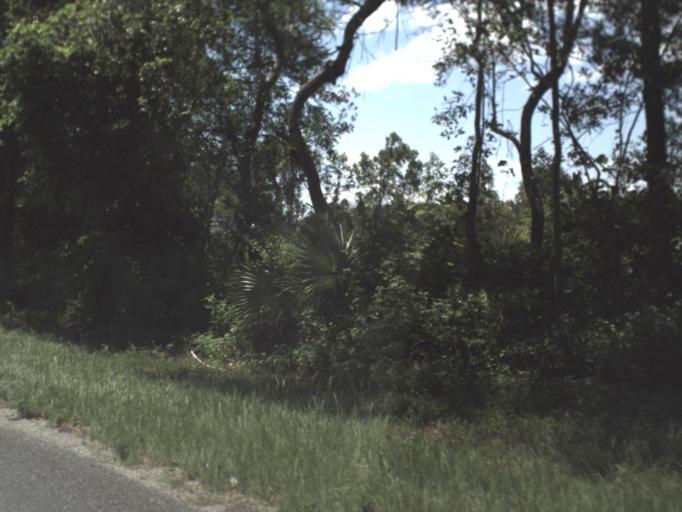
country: US
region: Florida
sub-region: Lafayette County
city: Mayo
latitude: 30.1292
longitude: -83.2958
